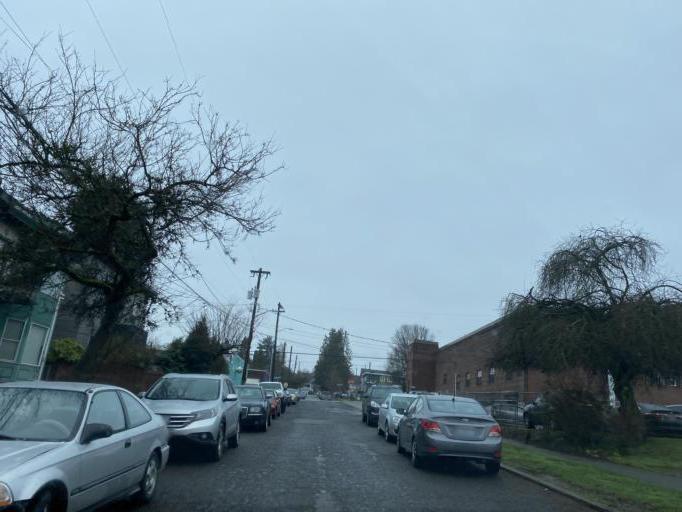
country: US
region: Washington
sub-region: King County
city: Seattle
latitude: 47.5984
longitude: -122.2963
